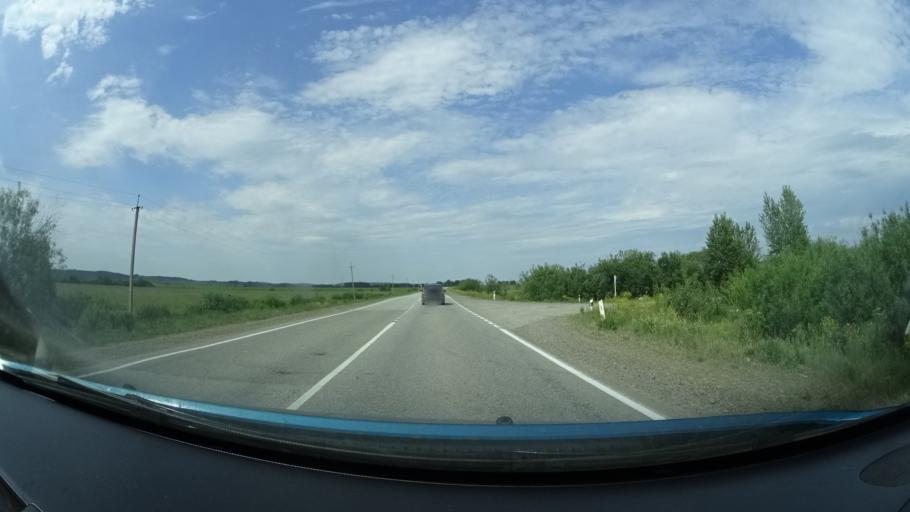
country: RU
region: Perm
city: Barda
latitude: 57.0562
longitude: 55.5433
